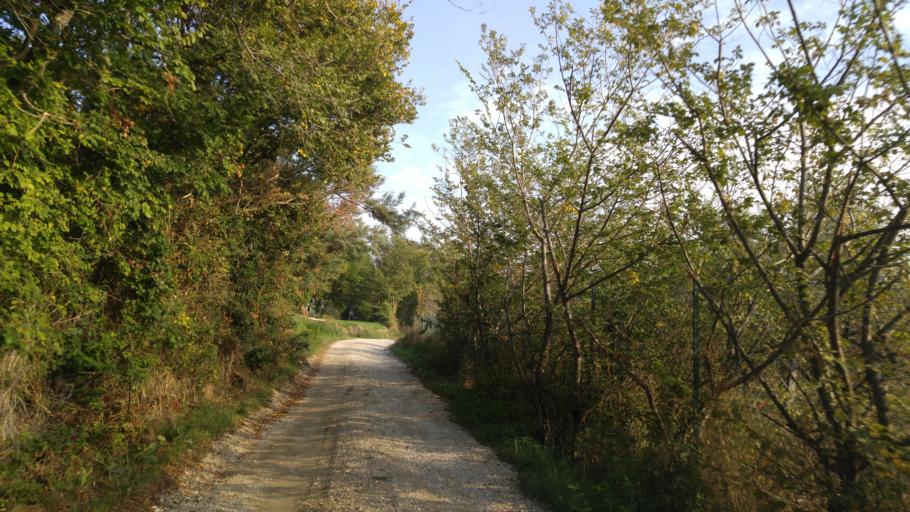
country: IT
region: The Marches
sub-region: Provincia di Pesaro e Urbino
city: Fenile
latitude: 43.8713
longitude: 12.9667
